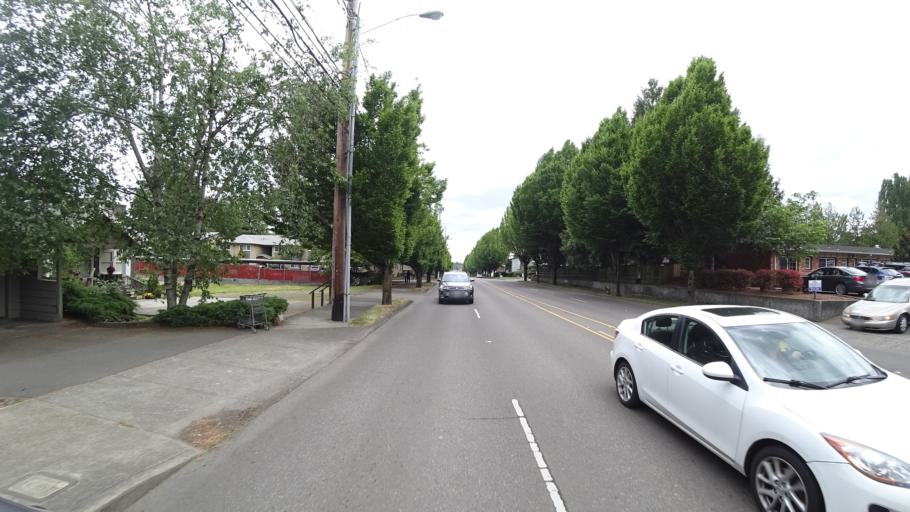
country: US
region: Oregon
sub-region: Washington County
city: Beaverton
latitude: 45.4766
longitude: -122.7986
